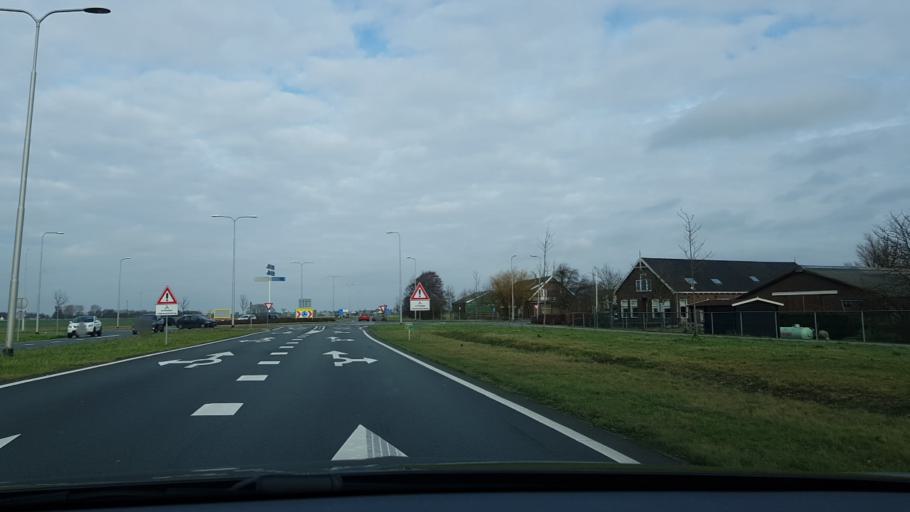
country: NL
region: South Holland
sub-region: Gemeente Kaag en Braassem
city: Leimuiden
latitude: 52.2099
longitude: 4.6790
